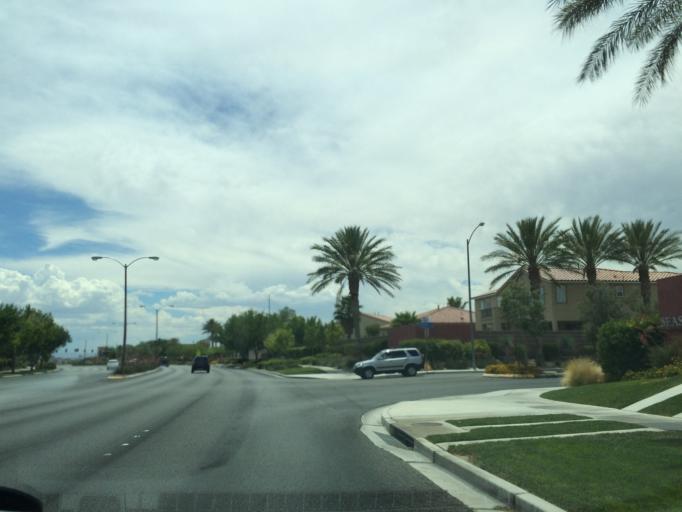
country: US
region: Nevada
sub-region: Clark County
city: North Las Vegas
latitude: 36.2791
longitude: -115.1795
